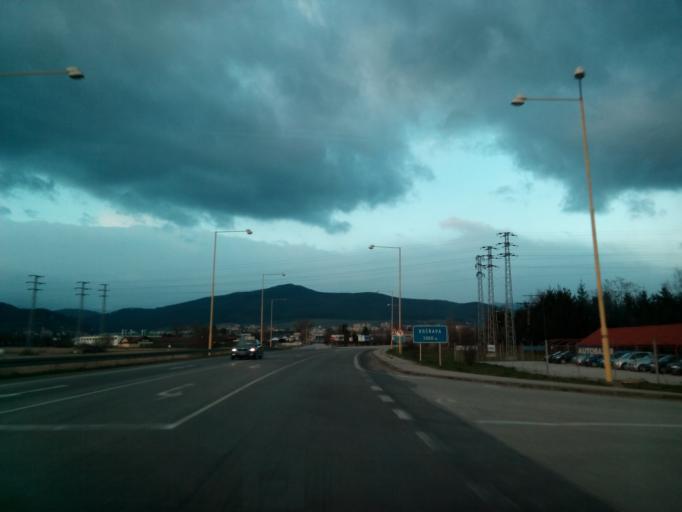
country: SK
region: Kosicky
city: Roznava
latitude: 48.6404
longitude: 20.5164
